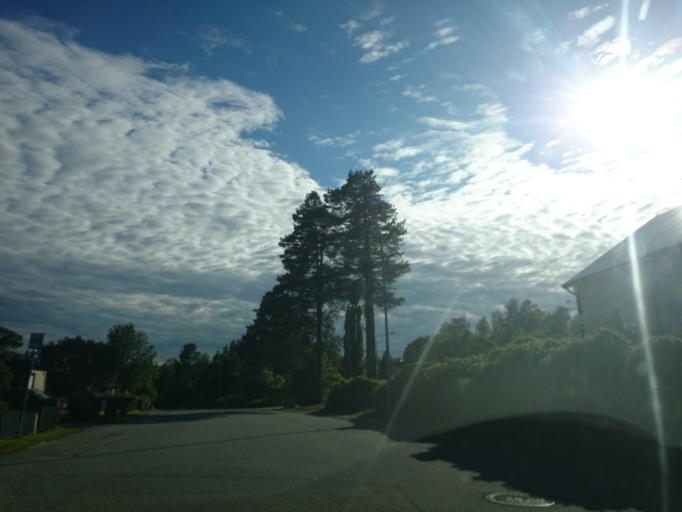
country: SE
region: Vaesternorrland
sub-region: Haernoesands Kommun
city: Haernoesand
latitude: 62.6452
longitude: 17.8894
